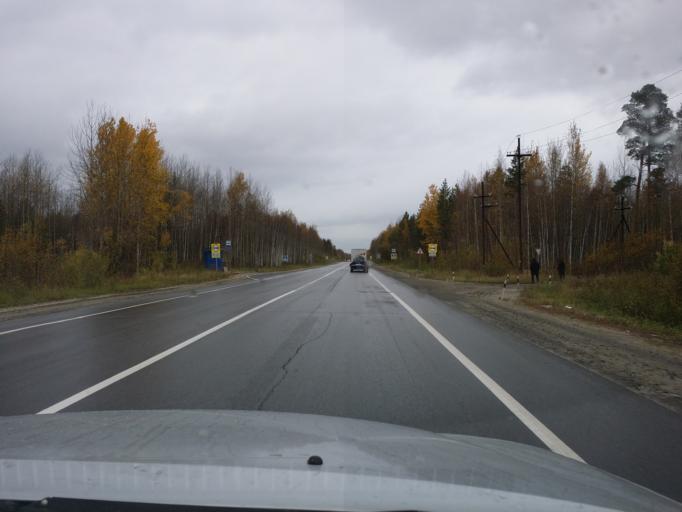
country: RU
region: Khanty-Mansiyskiy Avtonomnyy Okrug
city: Megion
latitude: 61.0958
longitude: 76.0721
